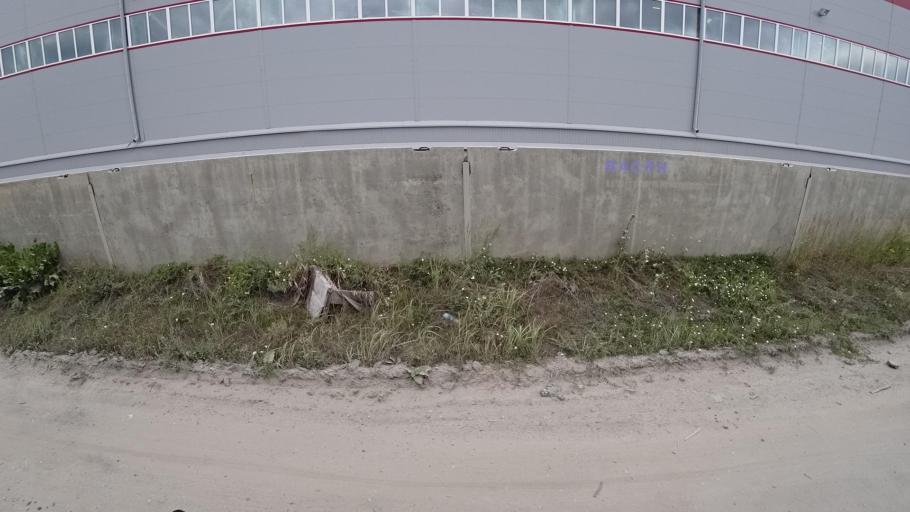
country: RU
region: Sverdlovsk
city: Kamyshlov
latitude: 56.8309
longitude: 62.7260
